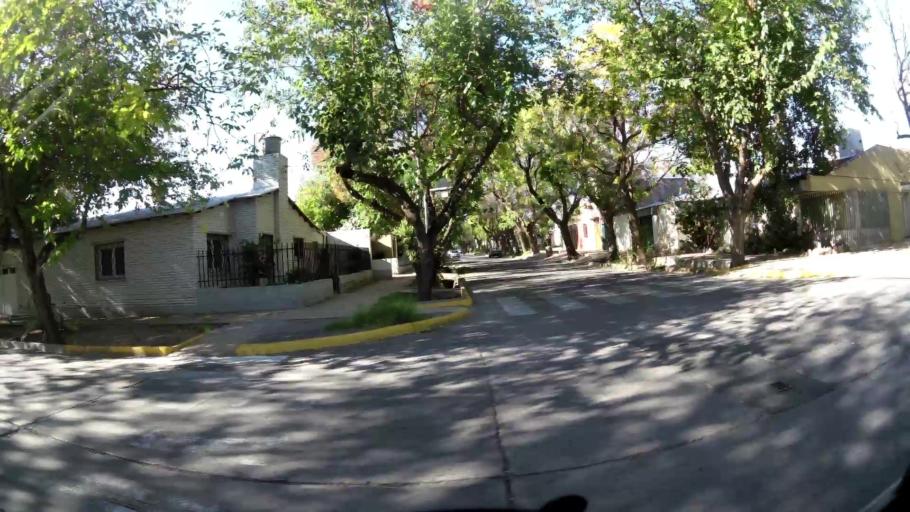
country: AR
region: Mendoza
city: Las Heras
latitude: -32.8665
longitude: -68.8519
